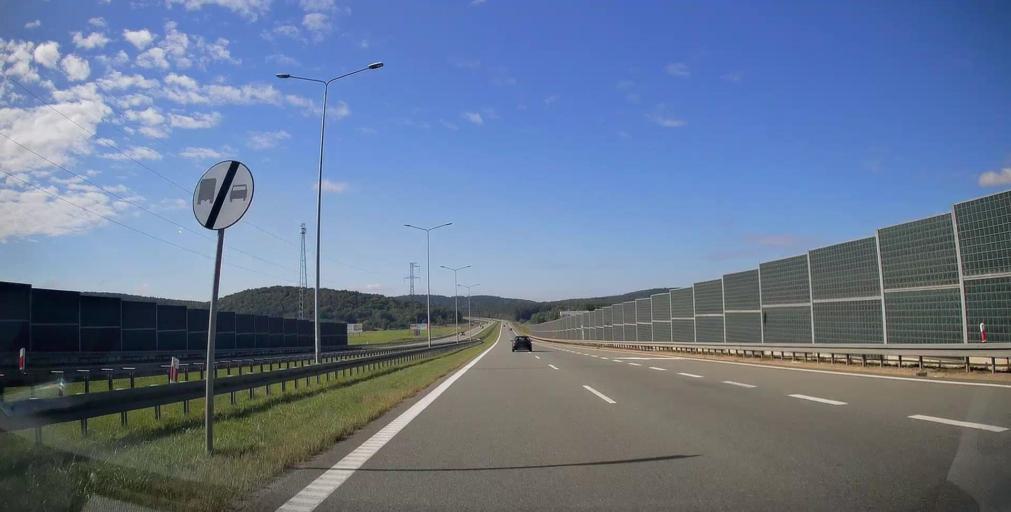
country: PL
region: Swietokrzyskie
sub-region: Powiat kielecki
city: Checiny
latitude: 50.8392
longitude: 20.4798
